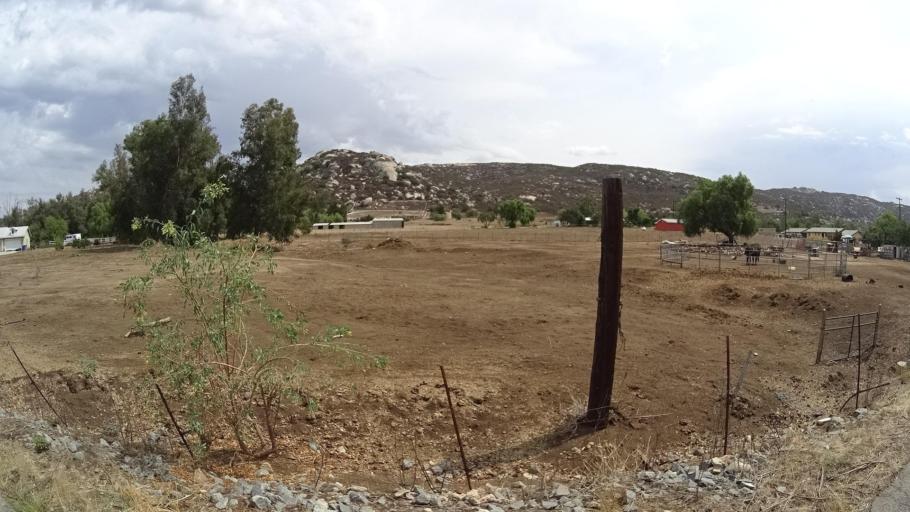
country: US
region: California
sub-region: San Diego County
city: Ramona
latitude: 33.0699
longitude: -116.8409
